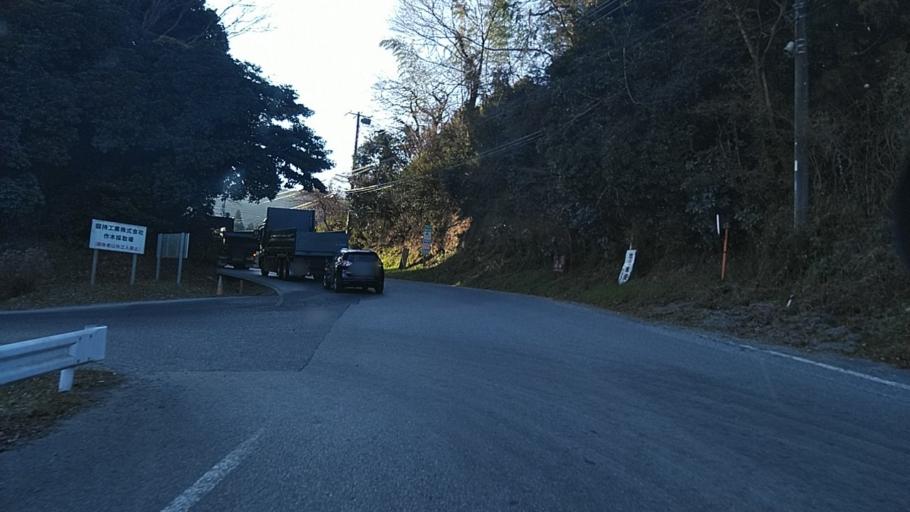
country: JP
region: Chiba
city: Kimitsu
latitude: 35.2712
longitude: 139.9198
